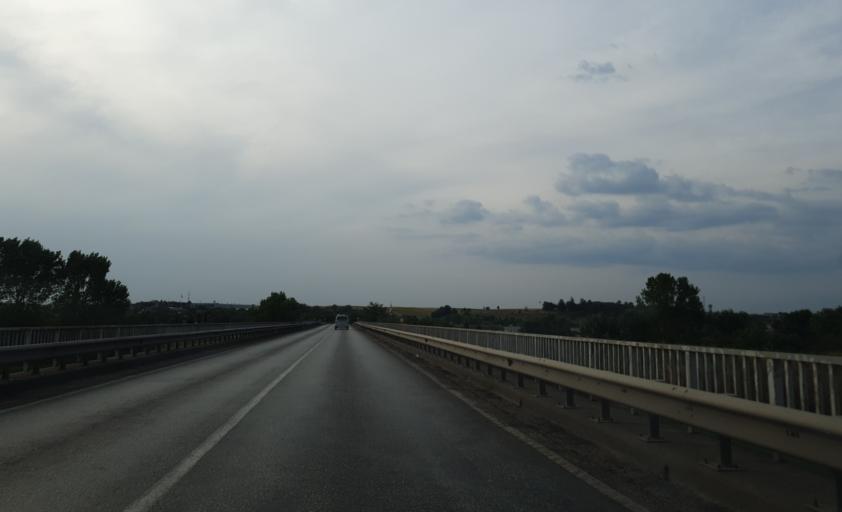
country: TR
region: Kirklareli
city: Babaeski
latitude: 41.3599
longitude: 27.1380
